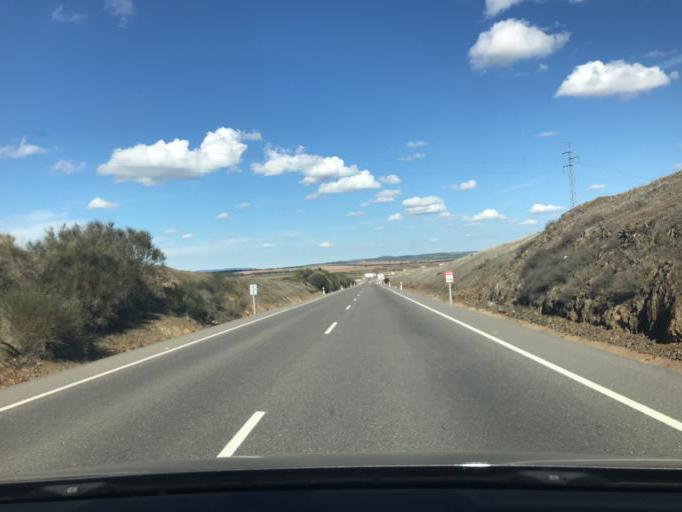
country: ES
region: Andalusia
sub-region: Province of Cordoba
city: Fuente Obejuna
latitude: 38.2718
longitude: -5.4302
